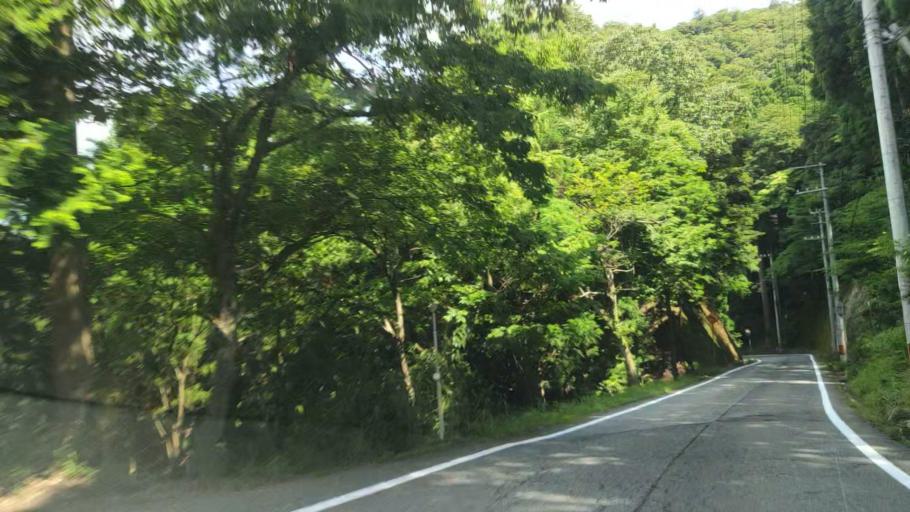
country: JP
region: Hyogo
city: Toyooka
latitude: 35.6408
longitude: 134.7658
